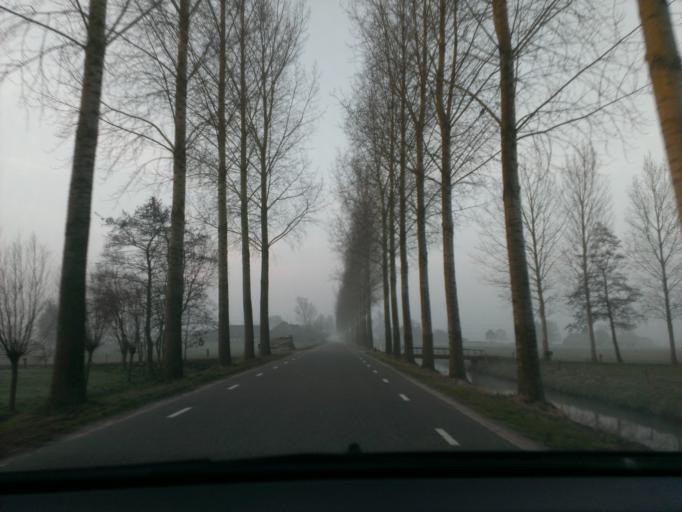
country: NL
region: Gelderland
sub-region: Gemeente Epe
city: Oene
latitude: 52.3012
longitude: 6.0383
